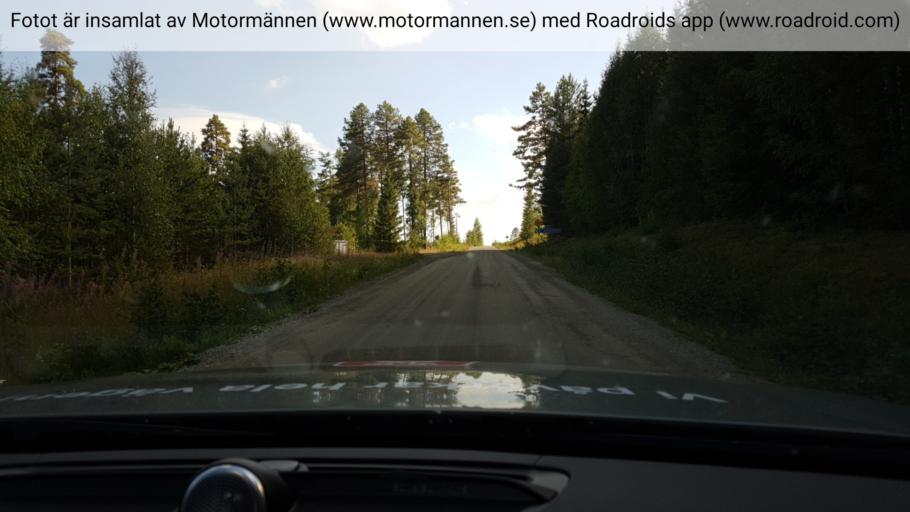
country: SE
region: Vaesternorrland
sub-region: Solleftea Kommun
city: As
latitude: 63.7881
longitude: 16.3913
